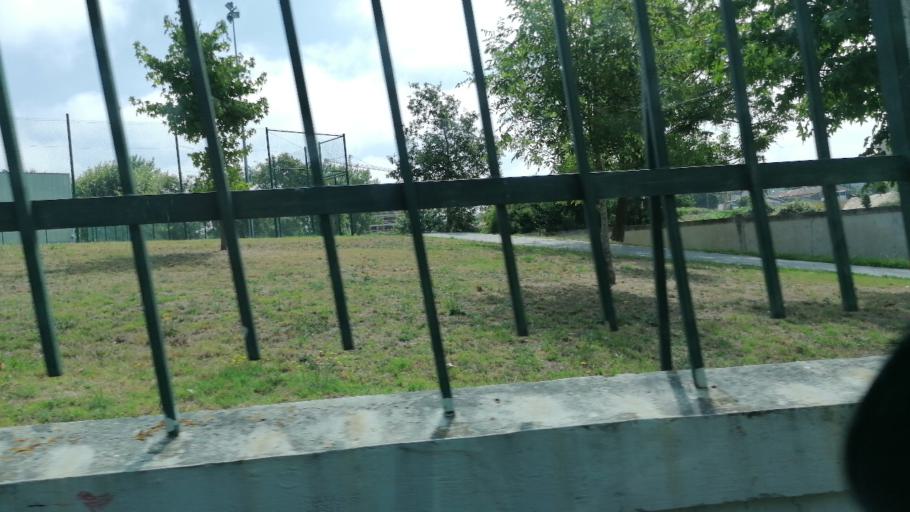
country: PT
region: Porto
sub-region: Matosinhos
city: Senhora da Hora
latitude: 41.1776
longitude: -8.6404
